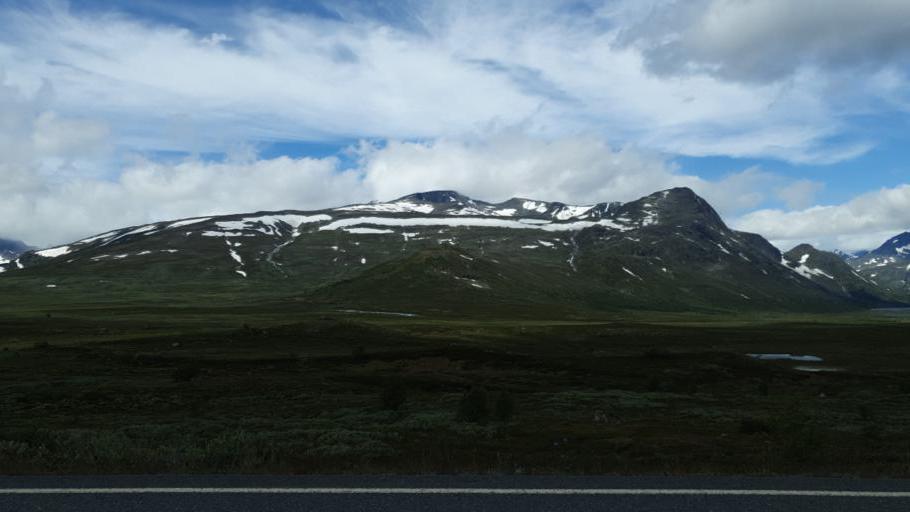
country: NO
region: Oppland
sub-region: Vang
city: Vang
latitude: 61.4561
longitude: 8.8062
